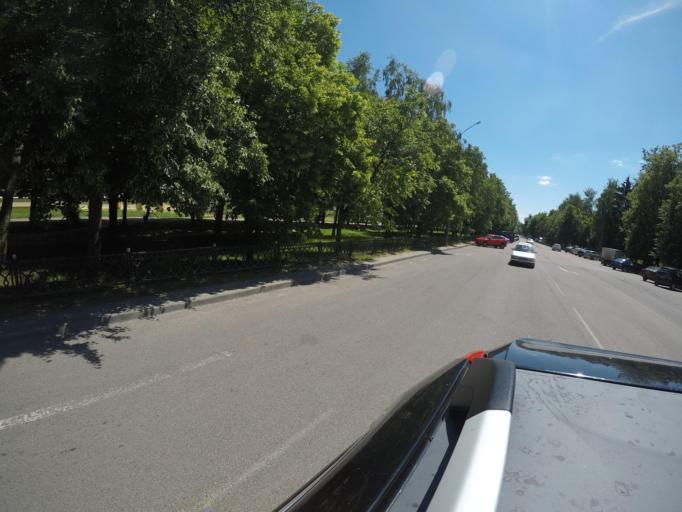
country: BY
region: Grodnenskaya
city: Hrodna
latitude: 53.6977
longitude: 23.8090
